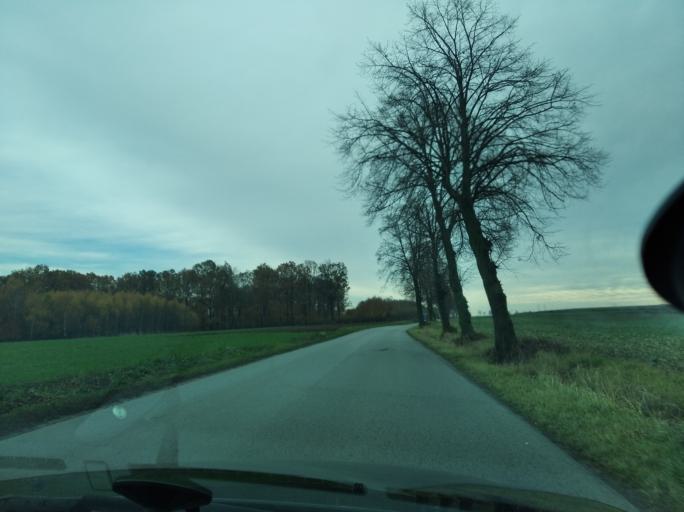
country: PL
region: Subcarpathian Voivodeship
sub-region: Powiat lancucki
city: Wysoka
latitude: 50.0286
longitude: 22.2457
